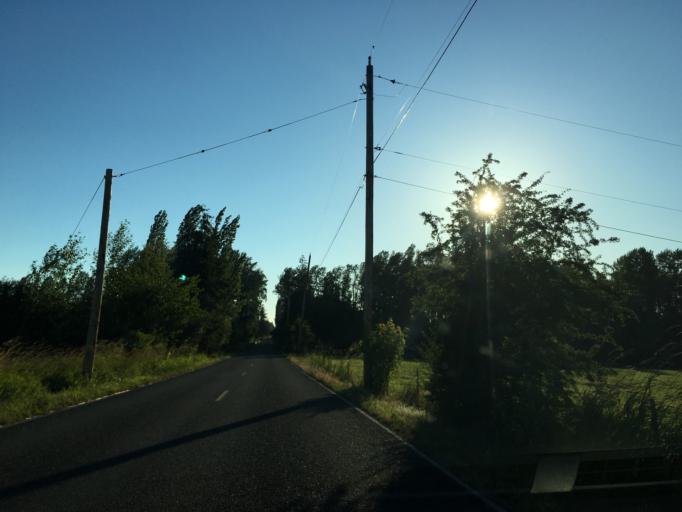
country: US
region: Washington
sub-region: Whatcom County
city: Sudden Valley
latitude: 48.8181
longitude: -122.3360
